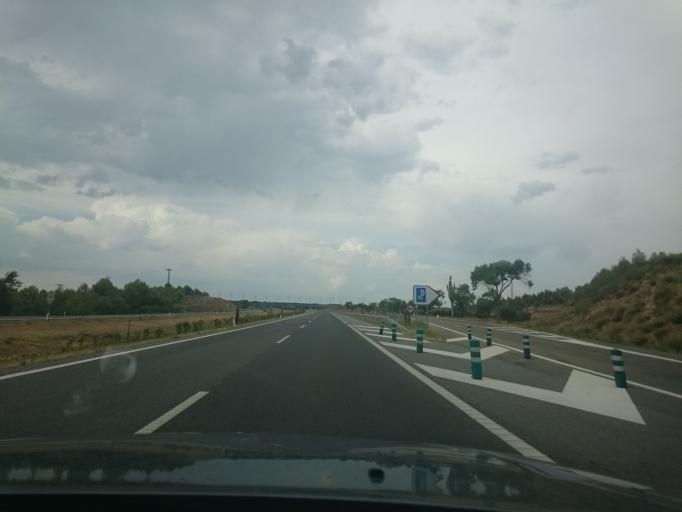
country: ES
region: Navarre
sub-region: Provincia de Navarra
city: Murchante
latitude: 42.0616
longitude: -1.6896
